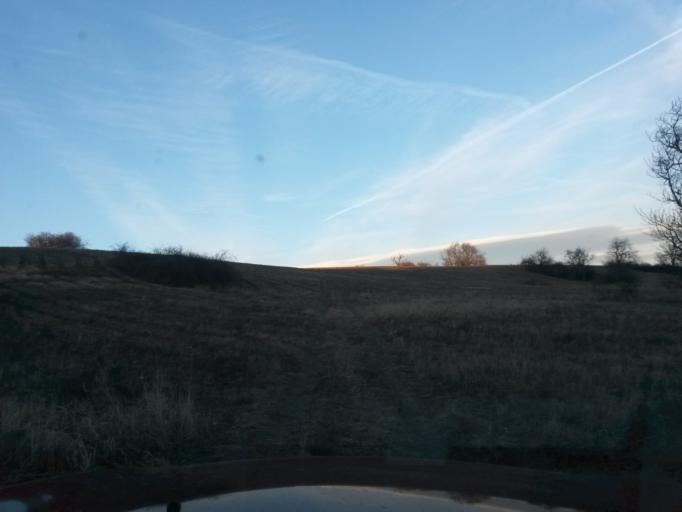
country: SK
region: Kosicky
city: Kosice
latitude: 48.7053
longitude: 21.3108
